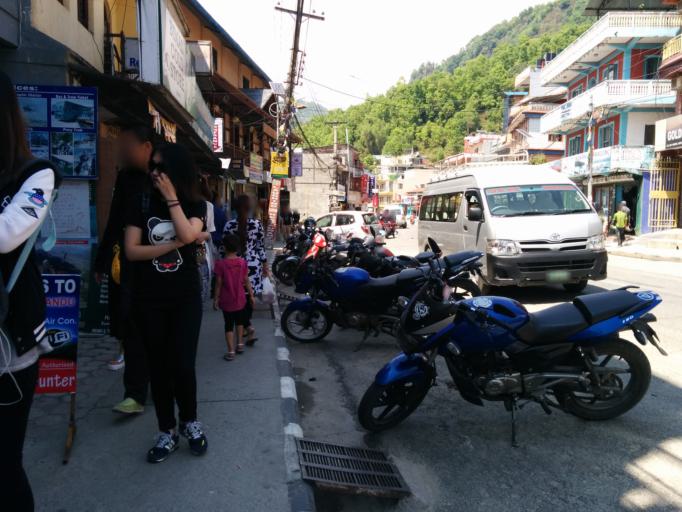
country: NP
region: Western Region
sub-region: Gandaki Zone
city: Pokhara
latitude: 28.2166
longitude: 83.9586
